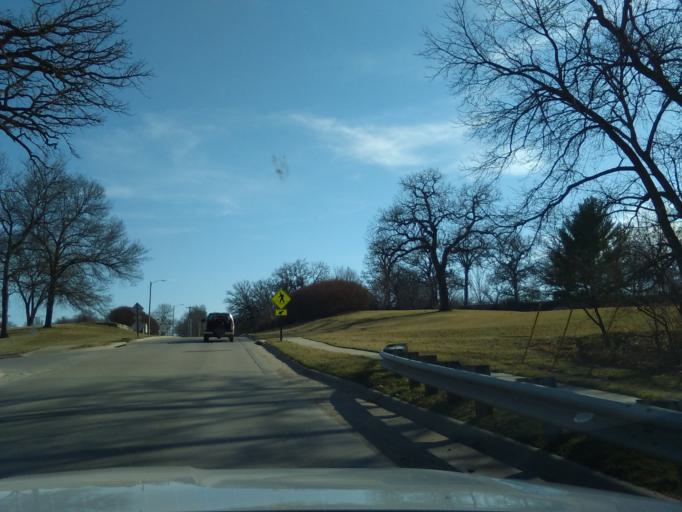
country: US
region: Nebraska
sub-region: Otoe County
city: Nebraska City
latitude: 40.6760
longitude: -95.8783
